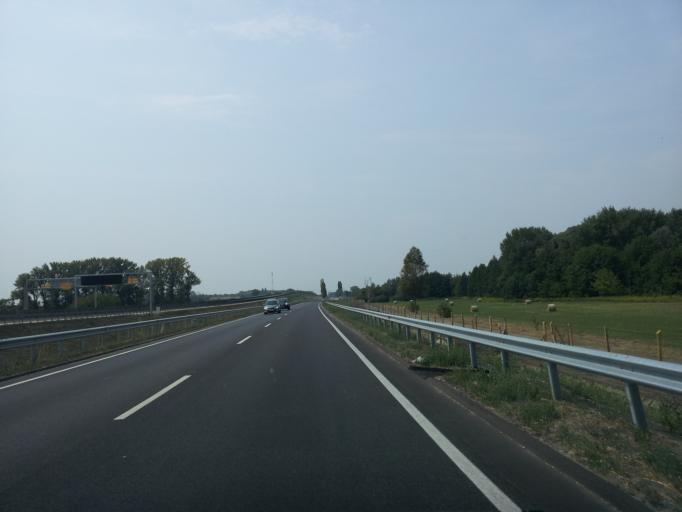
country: HU
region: Gyor-Moson-Sopron
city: Kony
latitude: 47.6291
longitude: 17.3257
